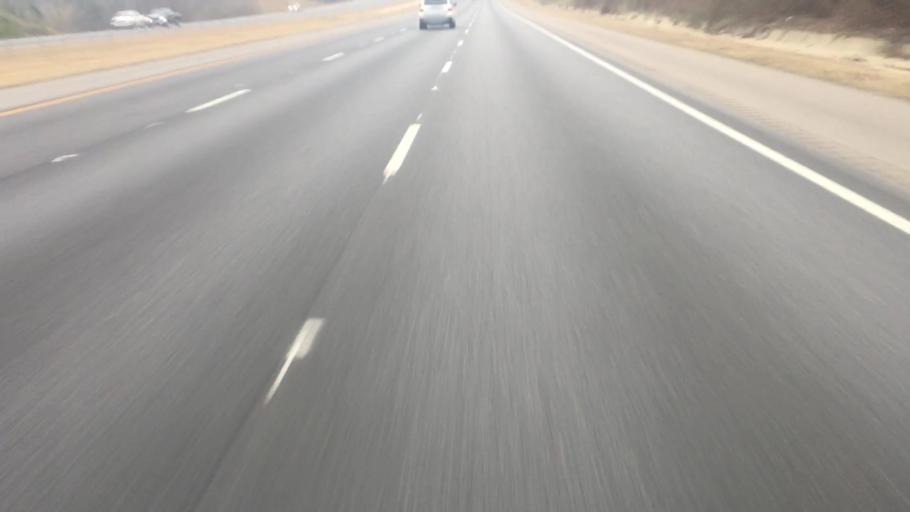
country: US
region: Alabama
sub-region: Jefferson County
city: Fultondale
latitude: 33.5874
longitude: -86.8424
